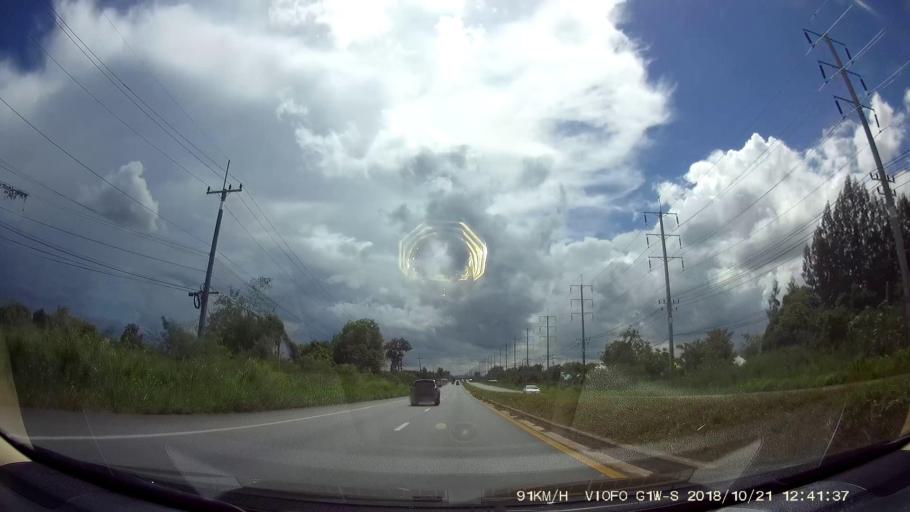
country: TH
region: Nakhon Ratchasima
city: Amphoe Sikhiu
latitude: 15.0103
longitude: 101.6866
